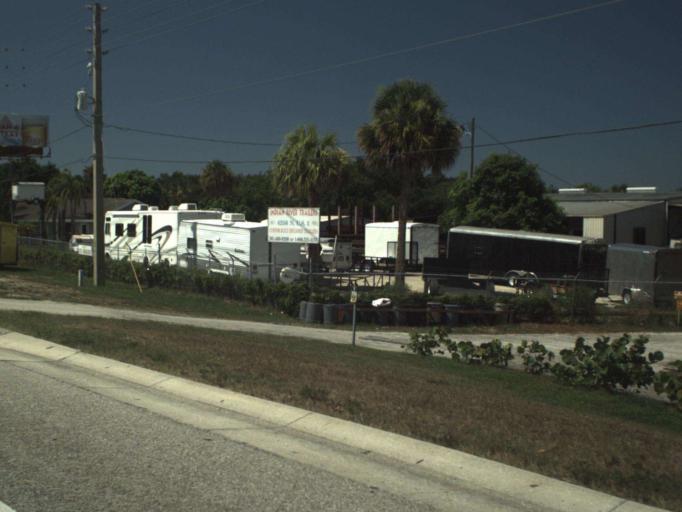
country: US
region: Florida
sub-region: Saint Lucie County
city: Lakewood Park
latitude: 27.5098
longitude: -80.3500
